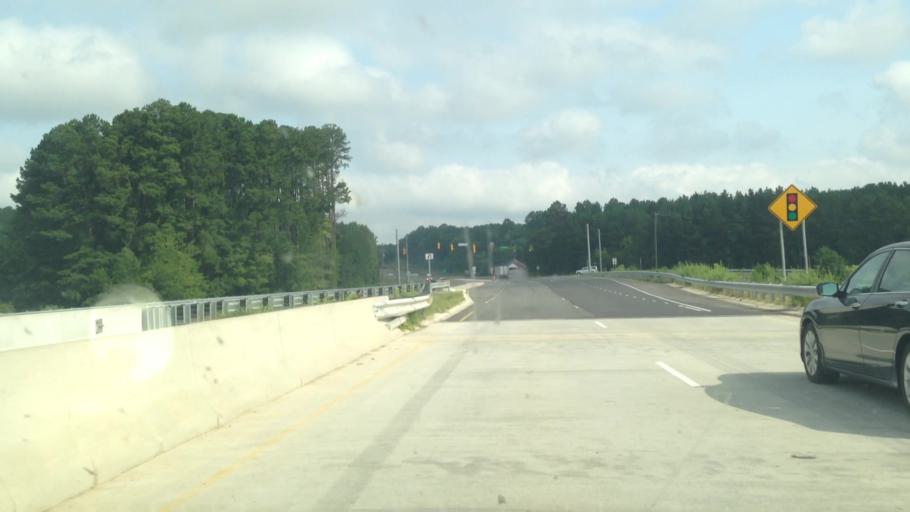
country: US
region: North Carolina
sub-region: Guilford County
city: Summerfield
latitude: 36.1739
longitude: -79.8813
